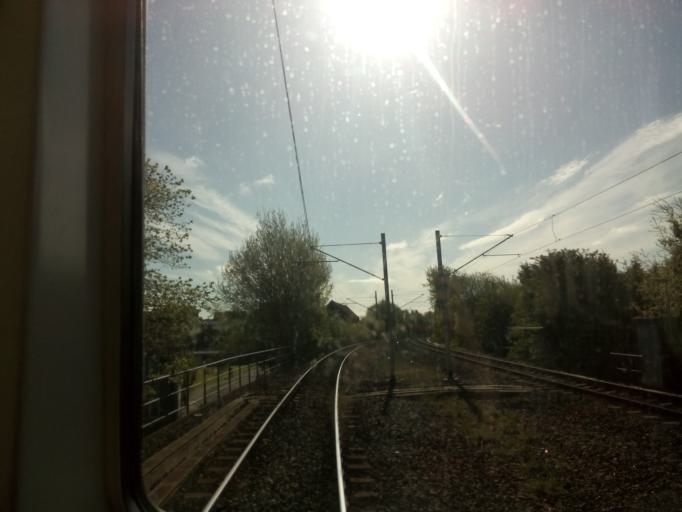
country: GB
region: England
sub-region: Newcastle upon Tyne
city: Gosforth
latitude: 55.0142
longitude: -1.6348
